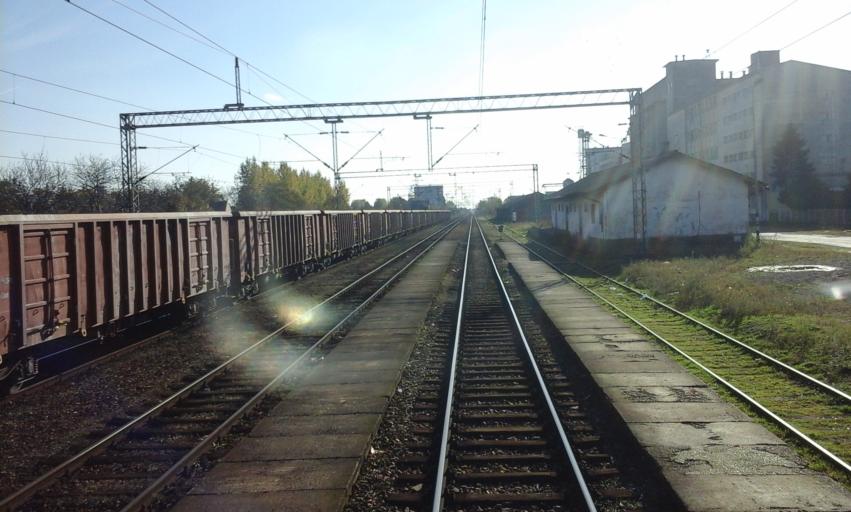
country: RS
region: Autonomna Pokrajina Vojvodina
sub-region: Severnobacki Okrug
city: Backa Topola
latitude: 45.8177
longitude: 19.6496
